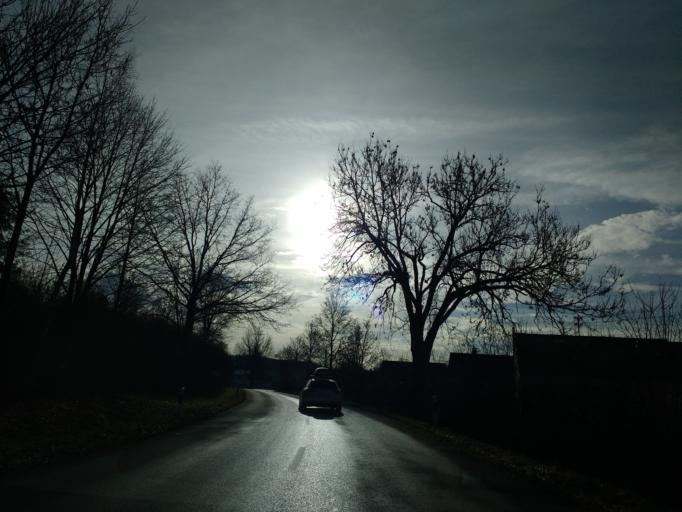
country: DE
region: Bavaria
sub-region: Swabia
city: Betzigau
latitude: 47.7400
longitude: 10.3822
